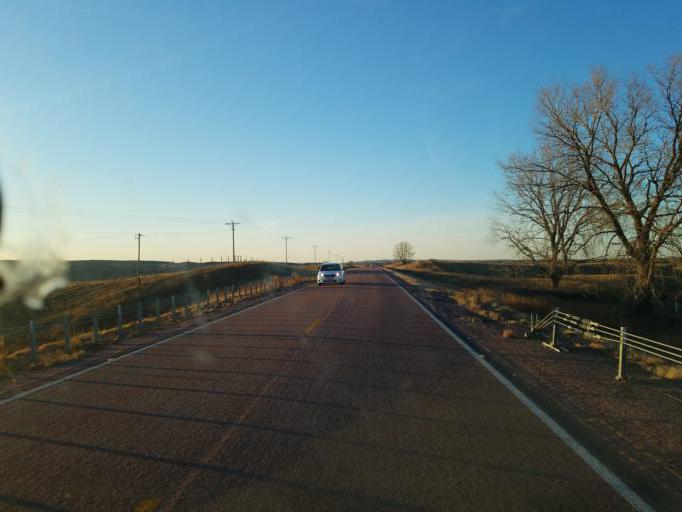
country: US
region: South Dakota
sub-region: Bon Homme County
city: Springfield
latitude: 42.7360
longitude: -97.9032
